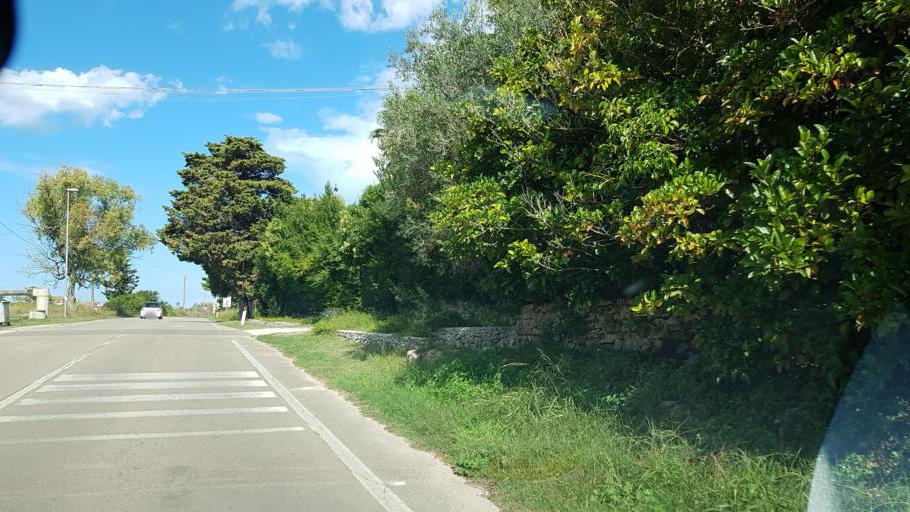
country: IT
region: Apulia
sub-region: Provincia di Lecce
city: Borgagne
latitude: 40.2261
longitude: 18.4417
